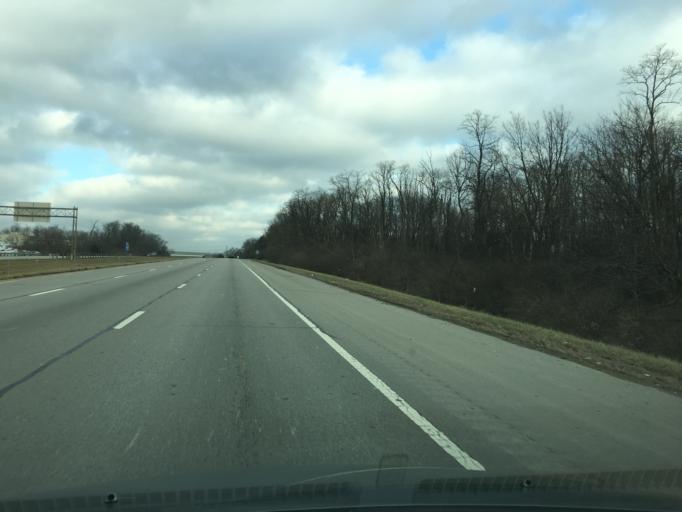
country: US
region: Ohio
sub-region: Hamilton County
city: Northgate
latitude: 39.2602
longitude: -84.5949
